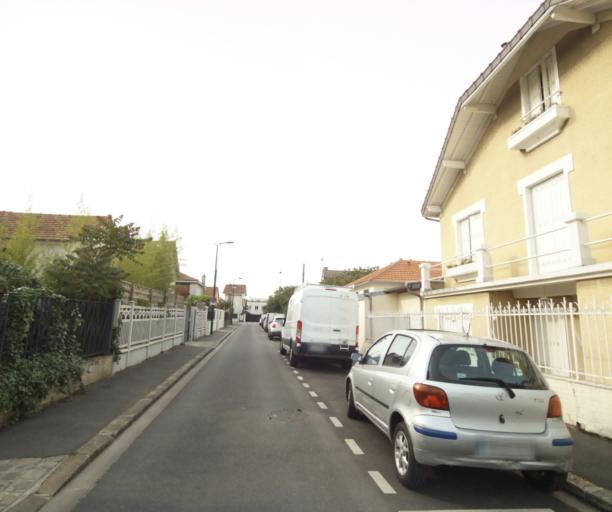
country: FR
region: Ile-de-France
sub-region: Departement des Hauts-de-Seine
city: Colombes
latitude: 48.9183
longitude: 2.2412
